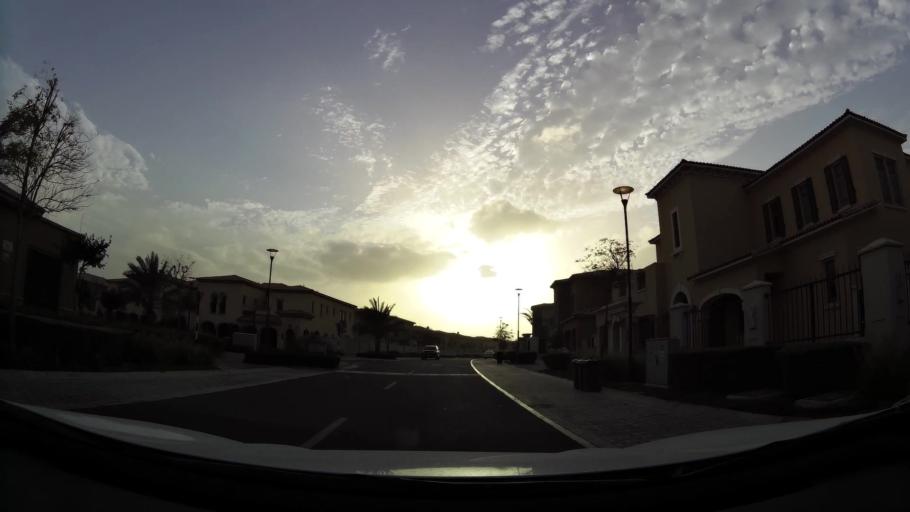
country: AE
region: Abu Dhabi
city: Abu Dhabi
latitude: 24.5349
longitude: 54.4322
